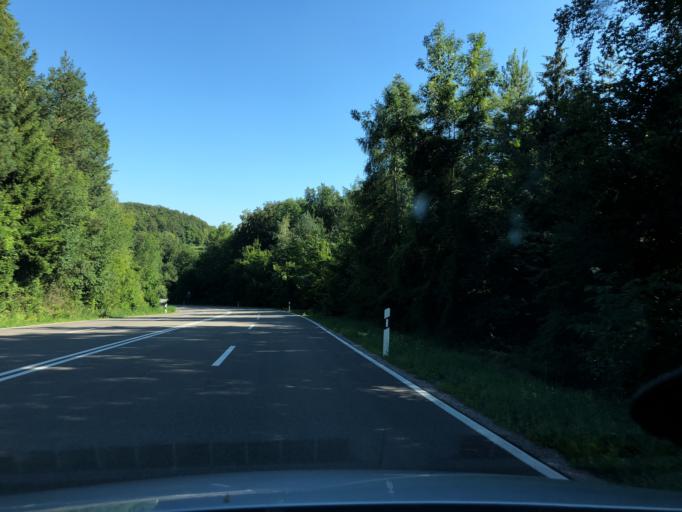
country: DE
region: Baden-Wuerttemberg
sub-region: Freiburg Region
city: Dogern
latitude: 47.6372
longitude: 8.1826
